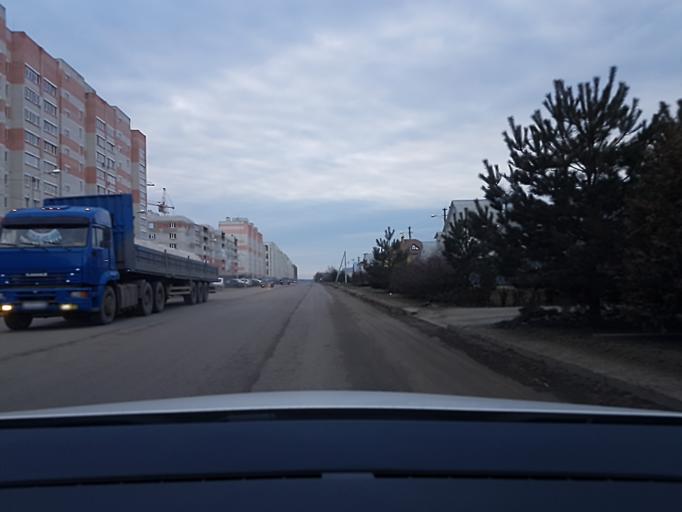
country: RU
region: Tambov
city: Tambov
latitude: 52.7769
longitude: 41.4001
